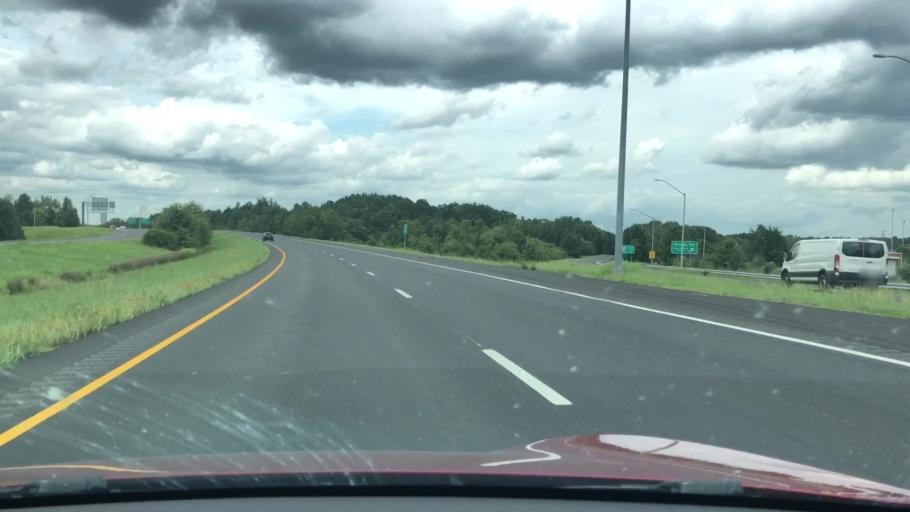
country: US
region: Maryland
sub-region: Wicomico County
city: Salisbury
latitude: 38.3652
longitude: -75.5370
